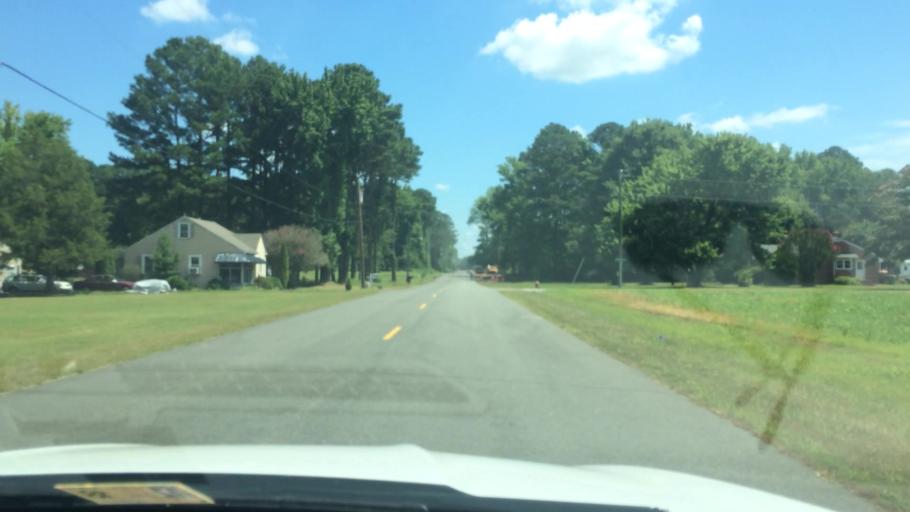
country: US
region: Virginia
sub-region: King William County
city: West Point
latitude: 37.5578
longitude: -76.8121
